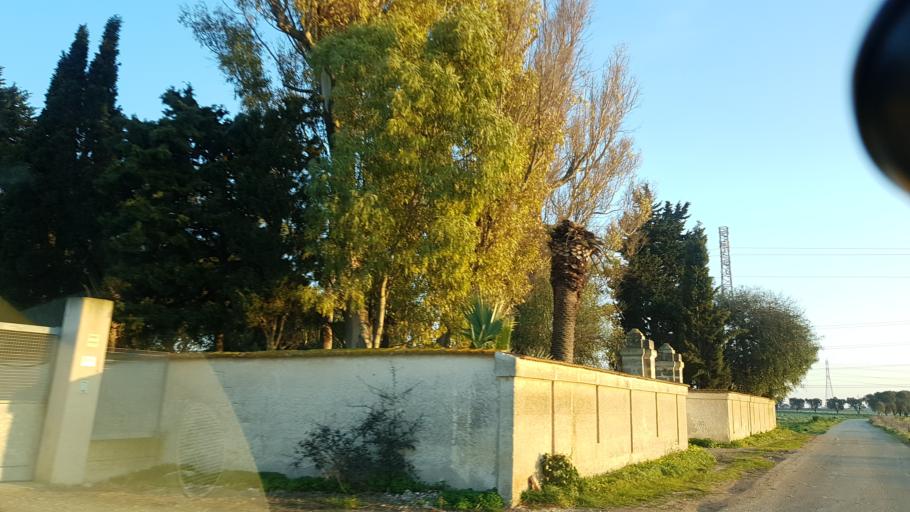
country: IT
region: Apulia
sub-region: Provincia di Brindisi
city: La Rosa
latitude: 40.6024
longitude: 17.9397
